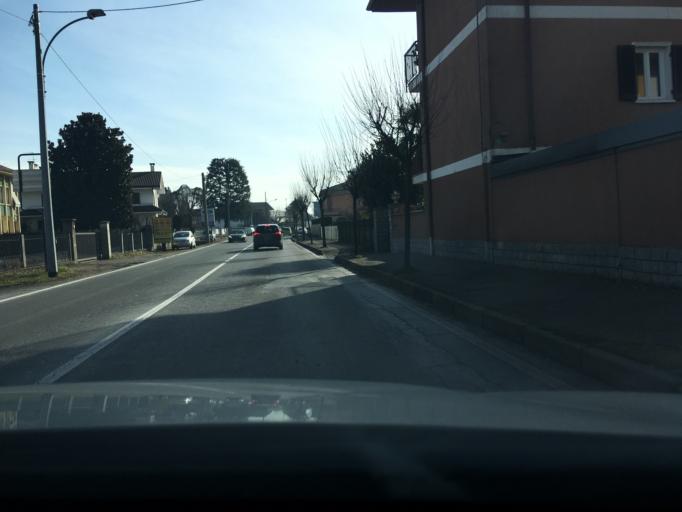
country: IT
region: Piedmont
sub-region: Provincia di Novara
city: Borgomanero
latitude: 45.6909
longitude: 8.4726
